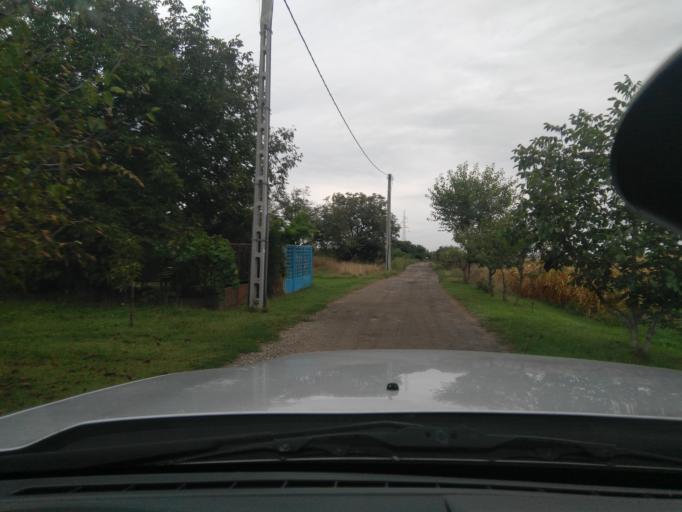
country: HU
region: Fejer
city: Martonvasar
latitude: 47.3522
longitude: 18.7631
